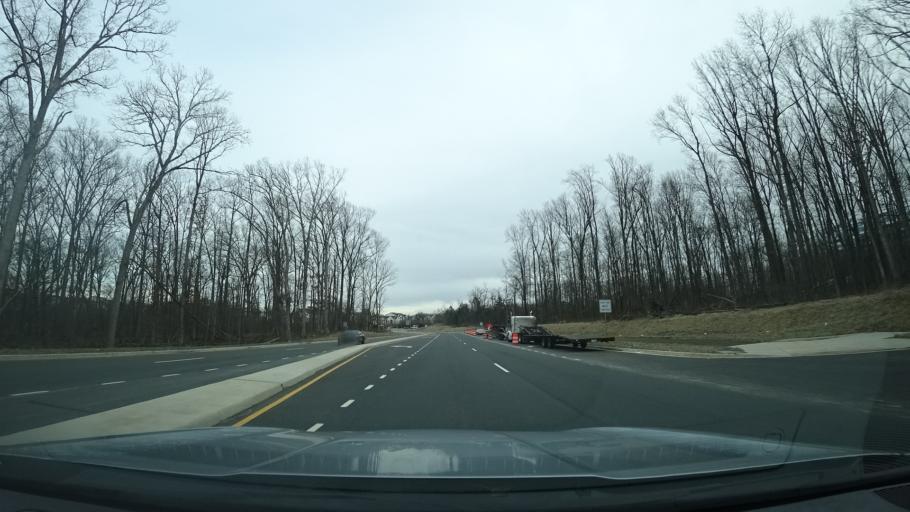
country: US
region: Virginia
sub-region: Loudoun County
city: Oak Grove
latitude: 38.9653
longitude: -77.4194
